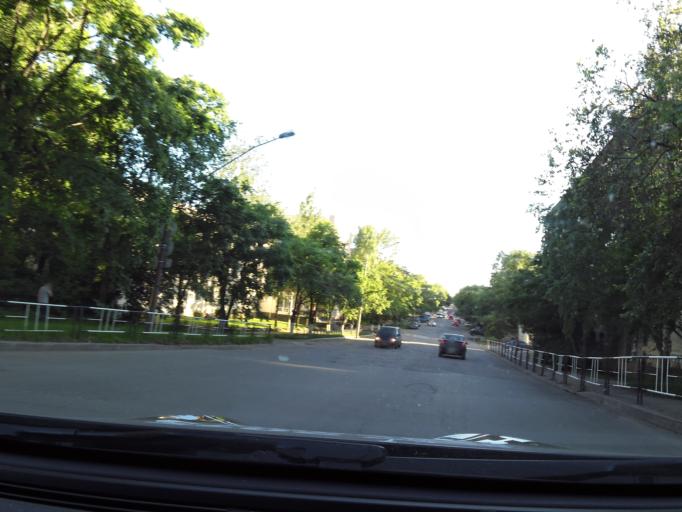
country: RU
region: Vologda
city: Vologda
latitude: 59.2089
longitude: 39.9092
